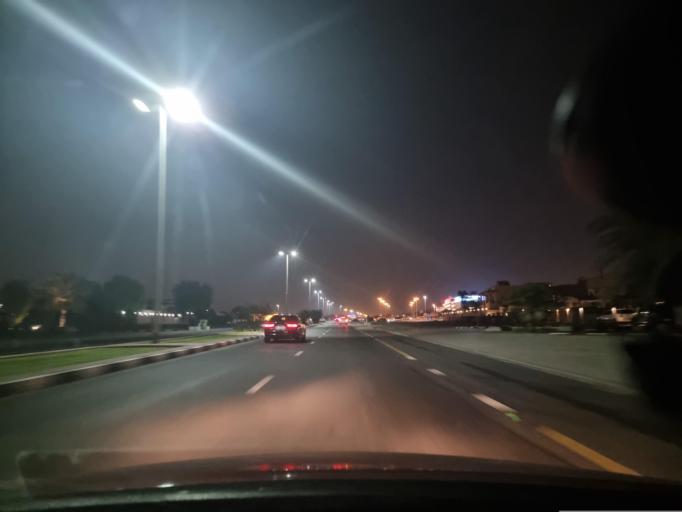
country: AE
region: Ash Shariqah
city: Sharjah
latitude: 25.3501
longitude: 55.4591
